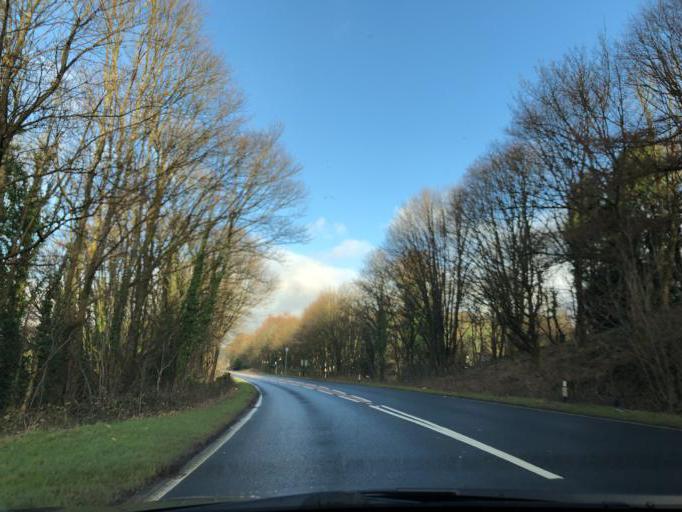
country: GB
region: England
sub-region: Cumbria
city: Grange-over-Sands
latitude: 54.2518
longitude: -2.9891
